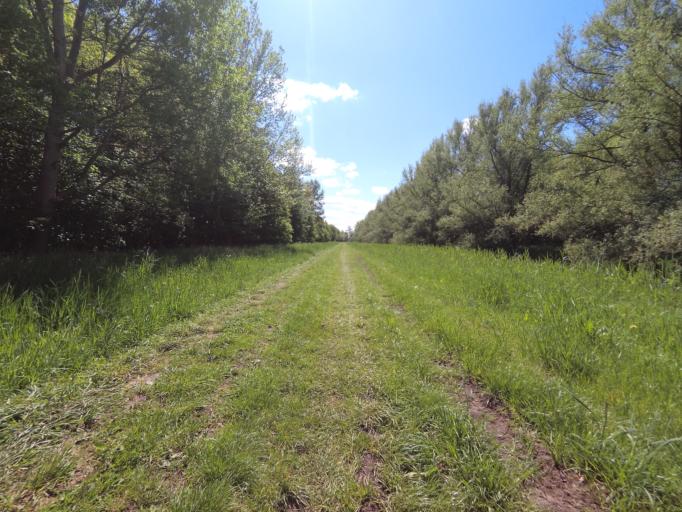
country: NL
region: Flevoland
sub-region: Gemeente Zeewolde
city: Zeewolde
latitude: 52.3036
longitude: 5.4925
